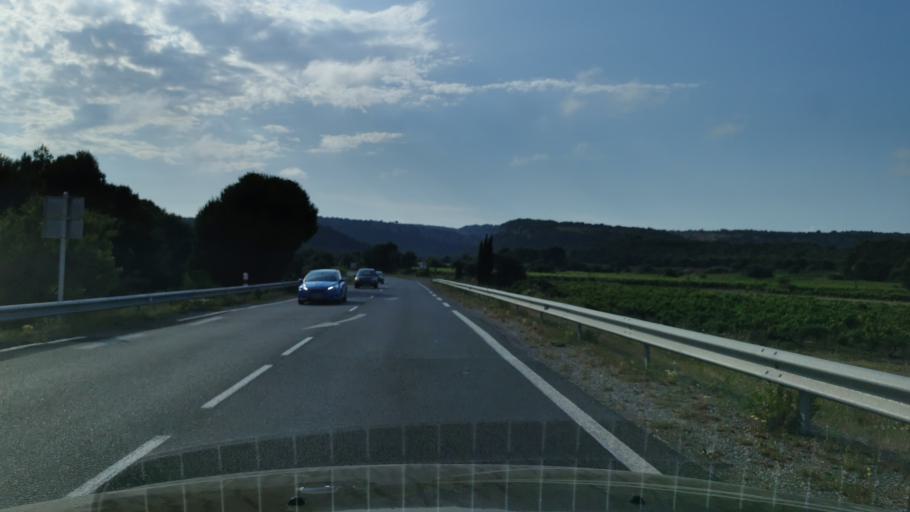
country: FR
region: Languedoc-Roussillon
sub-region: Departement de l'Aude
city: Gruissan
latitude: 43.1197
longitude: 3.1028
